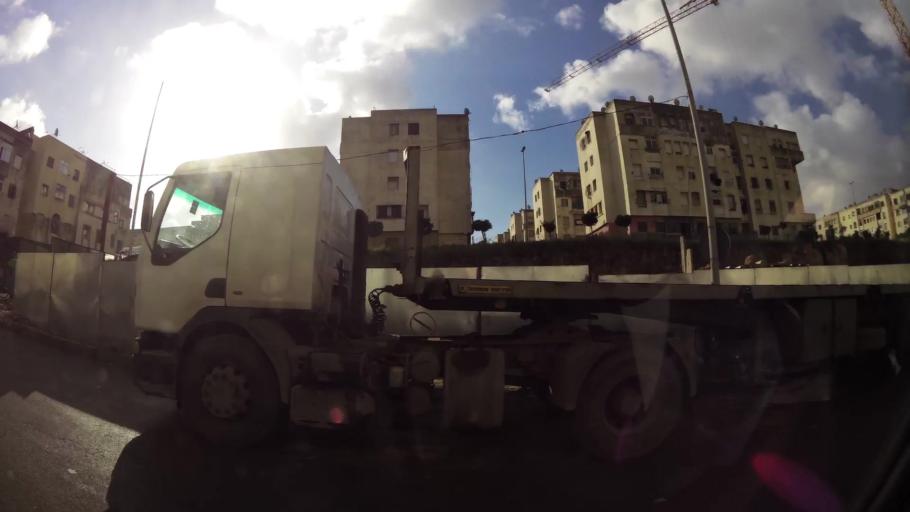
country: MA
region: Grand Casablanca
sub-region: Mediouna
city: Tit Mellil
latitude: 33.5964
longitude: -7.5345
